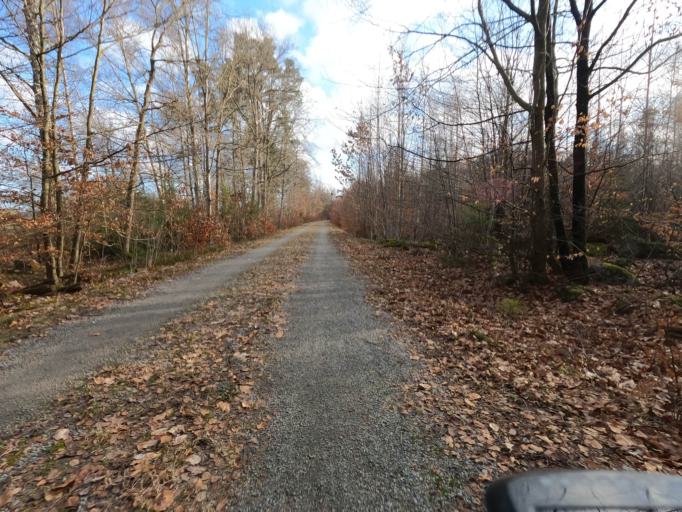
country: SE
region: Kronoberg
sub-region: Vaxjo Kommun
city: Gemla
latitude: 56.6643
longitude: 14.6212
